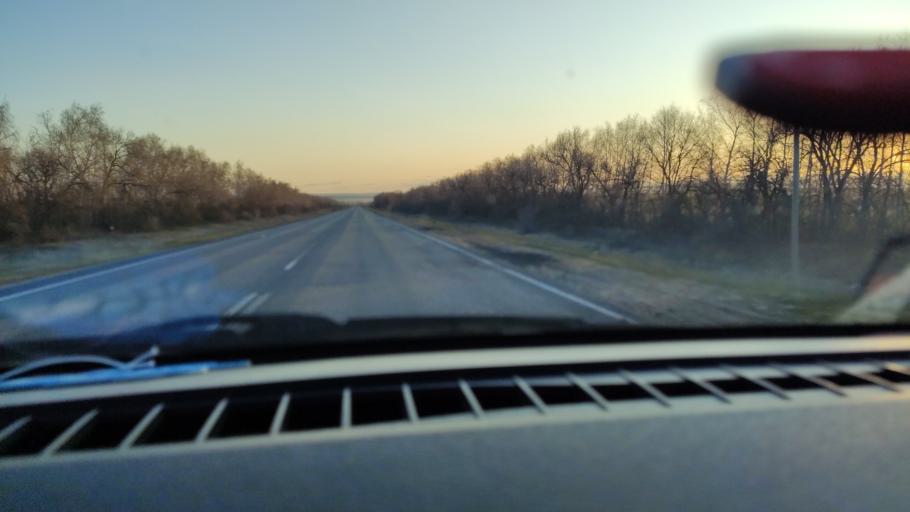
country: RU
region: Saratov
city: Sinodskoye
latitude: 51.9464
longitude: 46.6030
